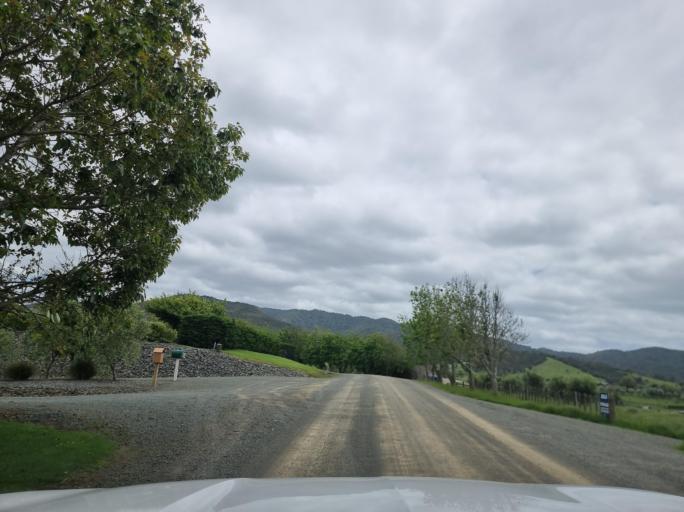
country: NZ
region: Auckland
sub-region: Auckland
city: Wellsford
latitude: -36.0940
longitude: 174.5321
